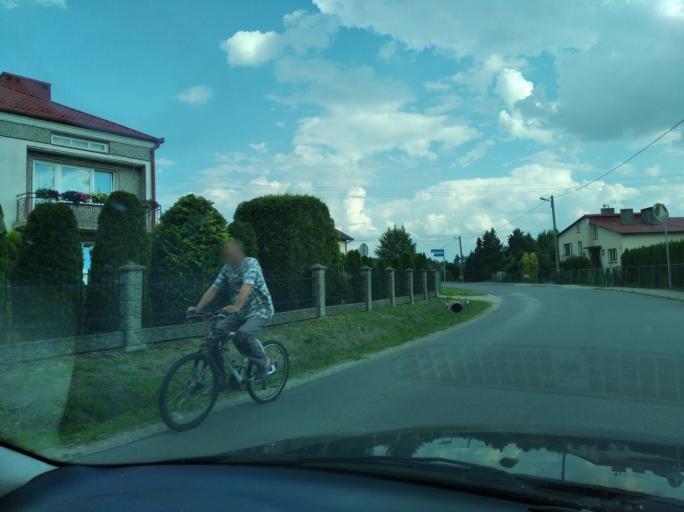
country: PL
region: Subcarpathian Voivodeship
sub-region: Powiat rzeszowski
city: Wysoka Glogowska
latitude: 50.1373
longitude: 22.0182
